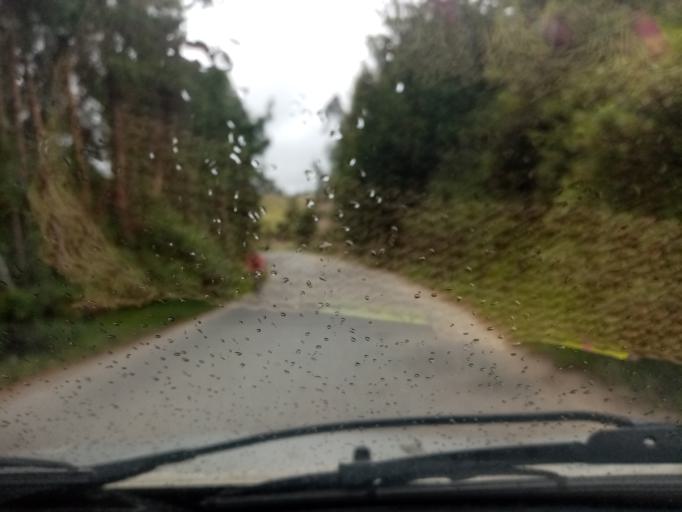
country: CO
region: Boyaca
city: Siachoque
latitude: 5.5698
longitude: -73.2543
